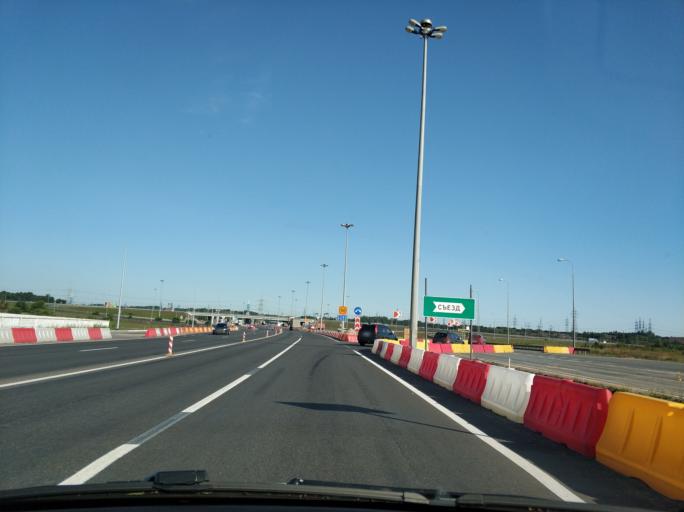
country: RU
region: Leningrad
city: Bugry
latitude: 60.0884
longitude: 30.3741
